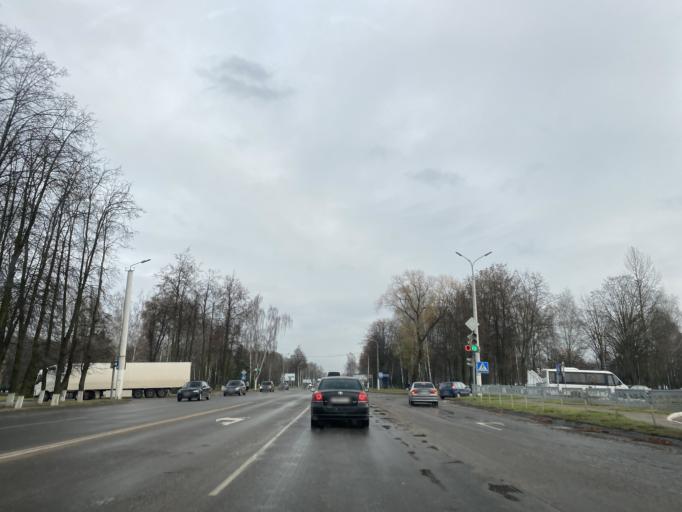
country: BY
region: Minsk
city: Horad Zhodzina
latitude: 54.0990
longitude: 28.3064
